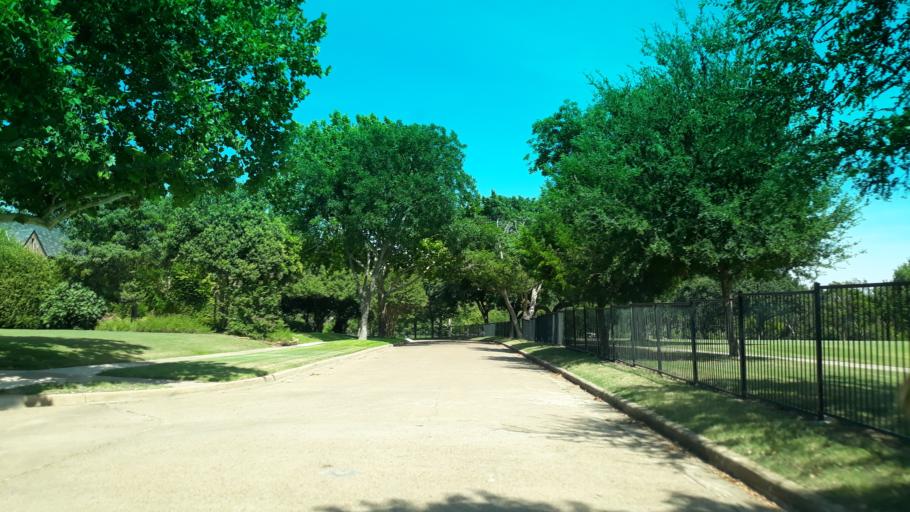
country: US
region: Texas
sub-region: Dallas County
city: Highland Park
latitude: 32.8150
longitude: -96.7468
